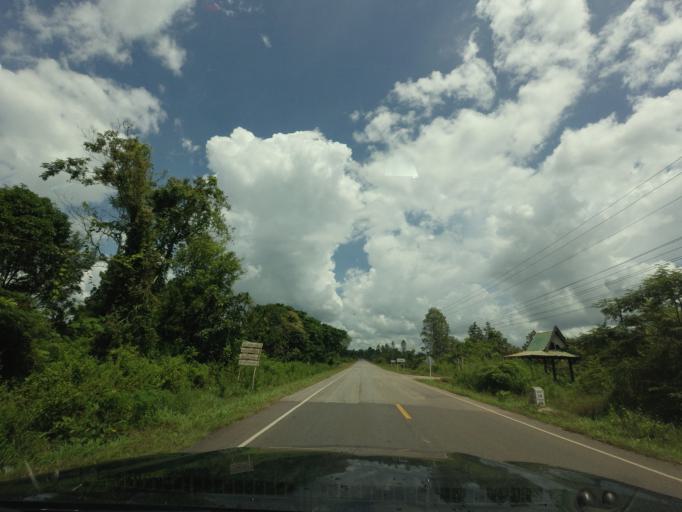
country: TH
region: Changwat Udon Thani
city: Phen
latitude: 17.5461
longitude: 102.8749
